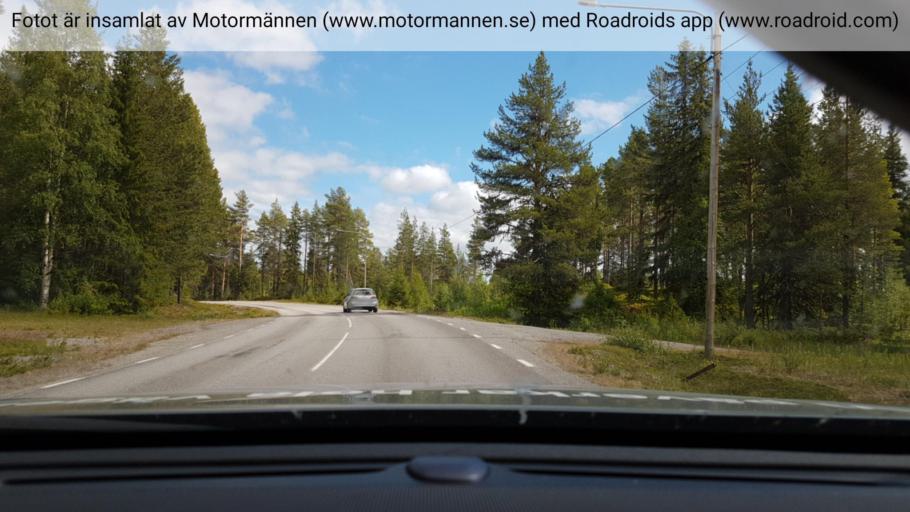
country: SE
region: Vaesterbotten
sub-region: Sorsele Kommun
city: Sorsele
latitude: 65.6011
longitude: 17.4858
